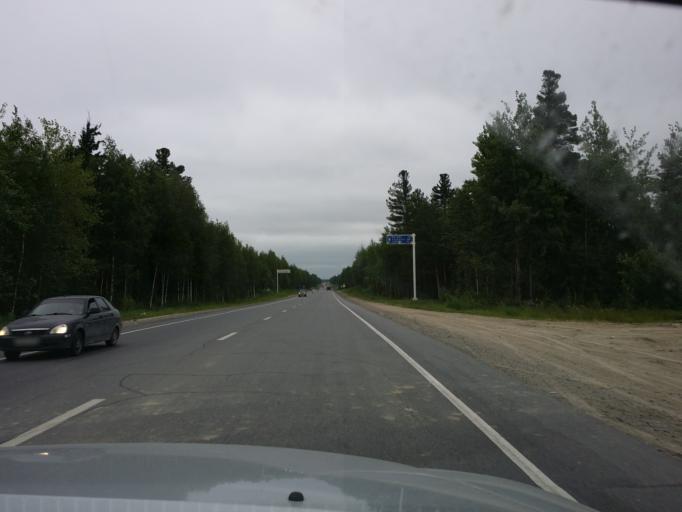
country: RU
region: Khanty-Mansiyskiy Avtonomnyy Okrug
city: Megion
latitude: 61.0578
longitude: 76.2955
